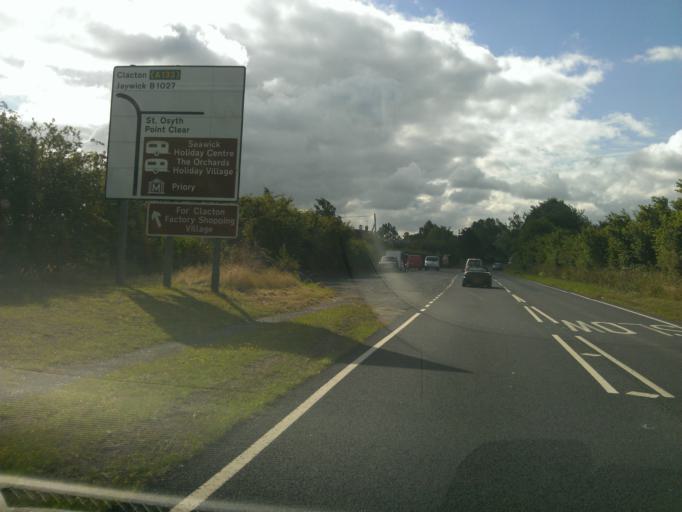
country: GB
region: England
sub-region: Essex
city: Saint Osyth
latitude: 51.8076
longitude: 1.0763
